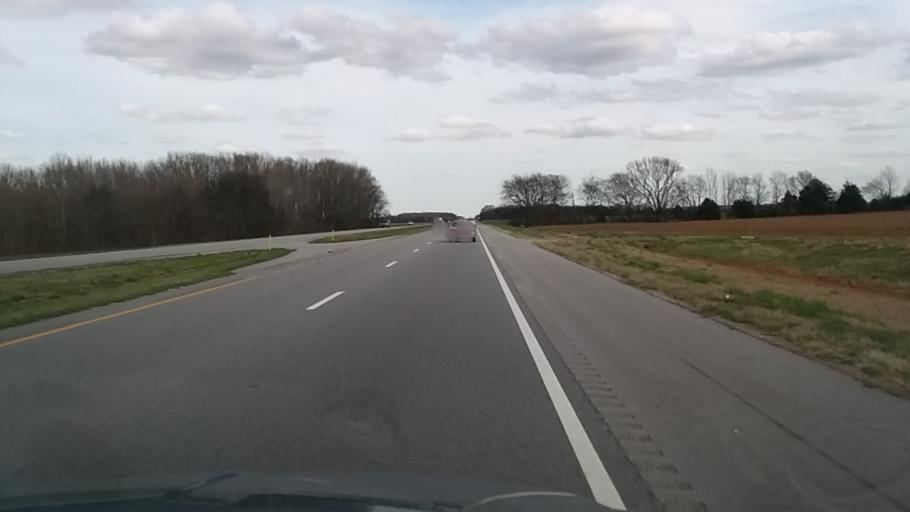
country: US
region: Alabama
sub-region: Lawrence County
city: Town Creek
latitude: 34.6833
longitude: -87.5068
